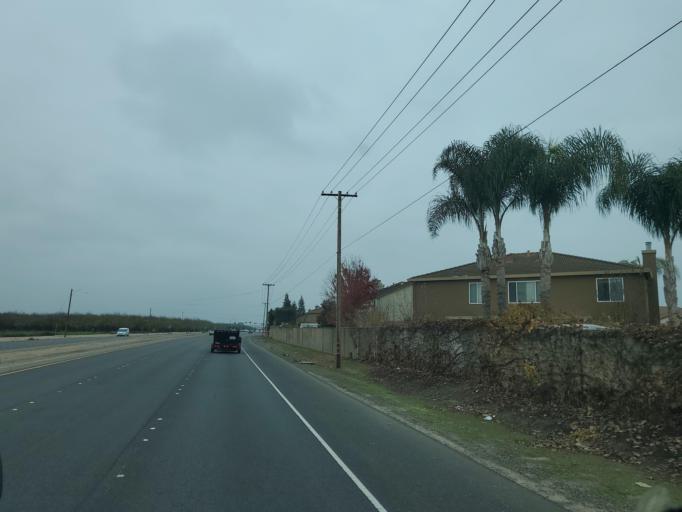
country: US
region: California
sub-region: Stanislaus County
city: Del Rio
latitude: 37.7006
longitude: -121.0176
